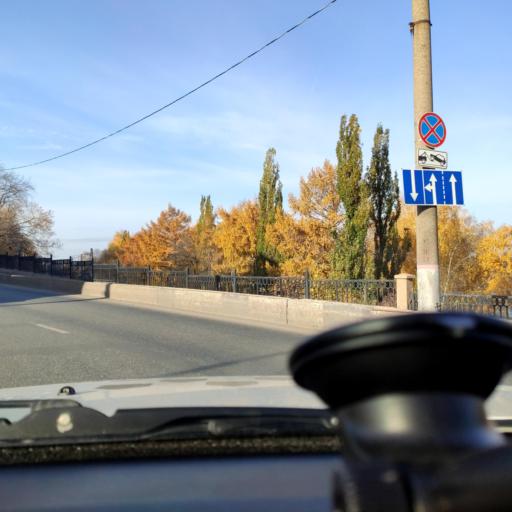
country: RU
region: Perm
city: Perm
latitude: 58.0191
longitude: 56.2469
